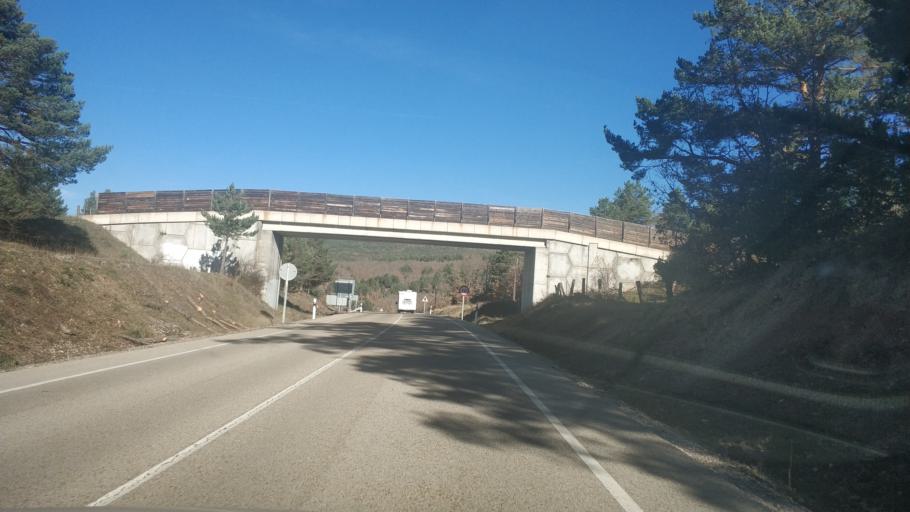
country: ES
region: Castille and Leon
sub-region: Provincia de Soria
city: Molinos de Duero
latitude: 41.8797
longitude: -2.7796
